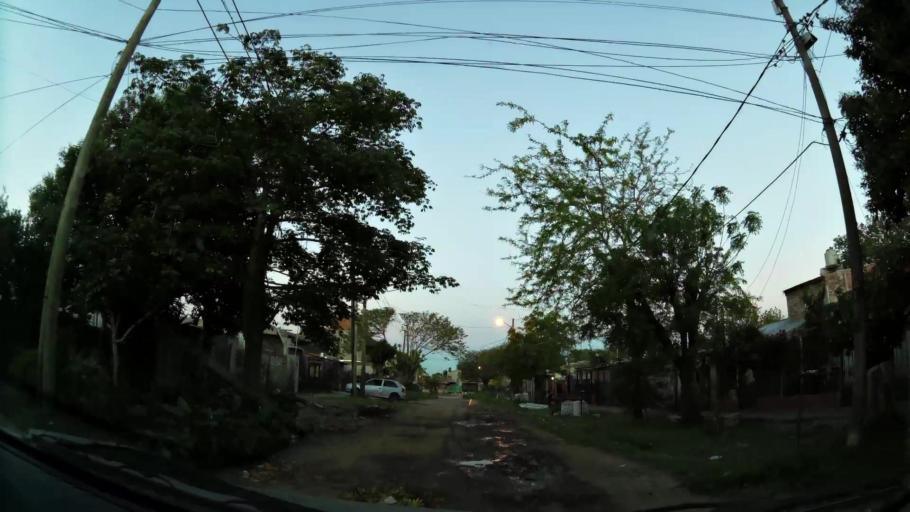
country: AR
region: Buenos Aires
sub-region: Partido de Almirante Brown
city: Adrogue
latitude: -34.7927
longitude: -58.3221
